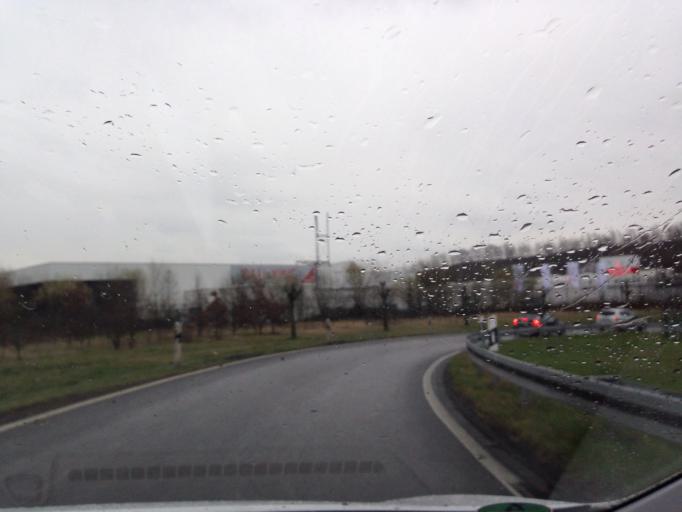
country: DE
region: North Rhine-Westphalia
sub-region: Regierungsbezirk Munster
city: Gladbeck
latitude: 51.5557
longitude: 6.9846
